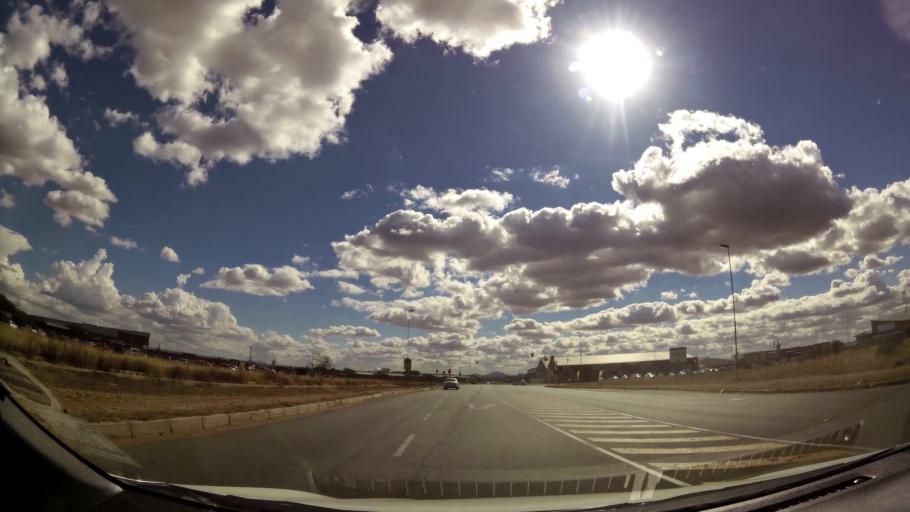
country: ZA
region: Limpopo
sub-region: Capricorn District Municipality
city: Polokwane
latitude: -23.8689
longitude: 29.4807
